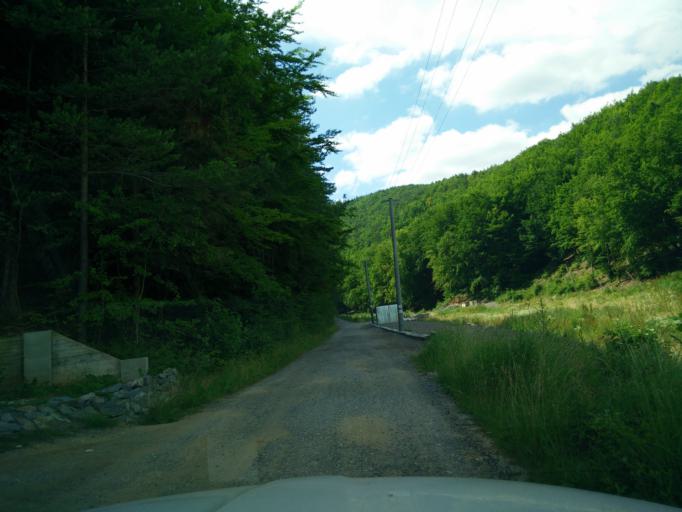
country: SK
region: Nitriansky
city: Bojnice
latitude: 48.8362
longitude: 18.5822
